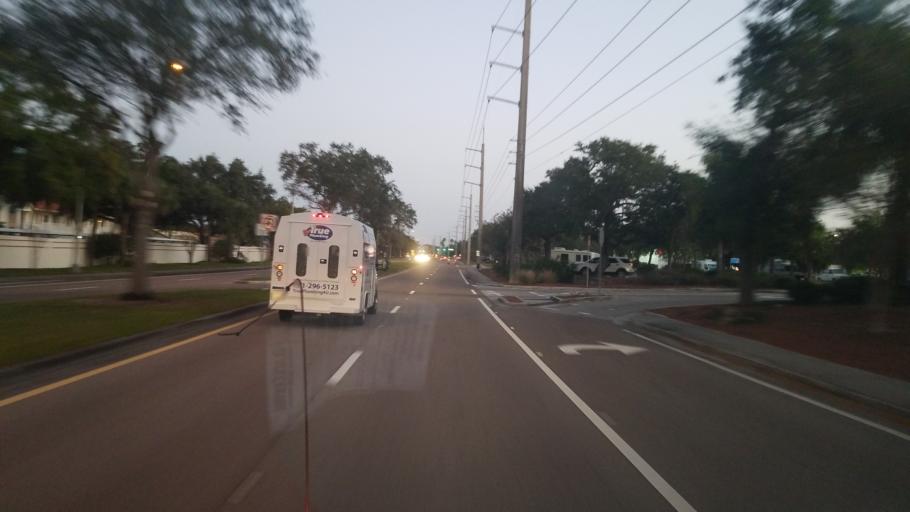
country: US
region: Florida
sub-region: Sarasota County
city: Lake Sarasota
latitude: 27.2916
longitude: -82.4520
